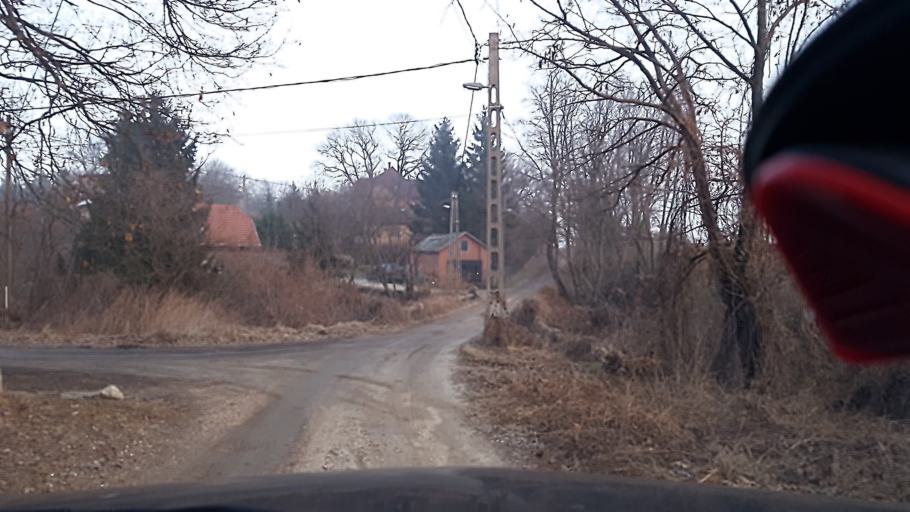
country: HU
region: Pest
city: Piliscsaba
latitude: 47.6421
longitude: 18.8240
